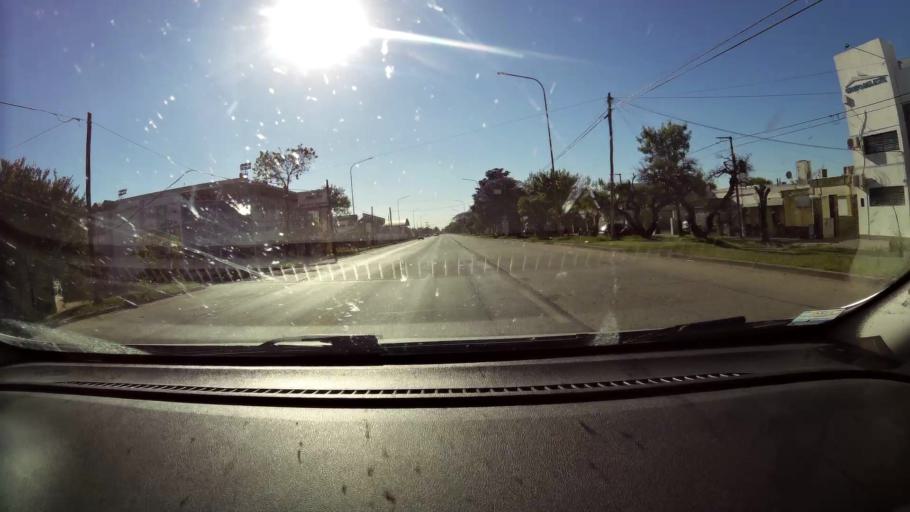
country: AR
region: Cordoba
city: San Francisco
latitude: -31.4175
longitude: -62.0776
